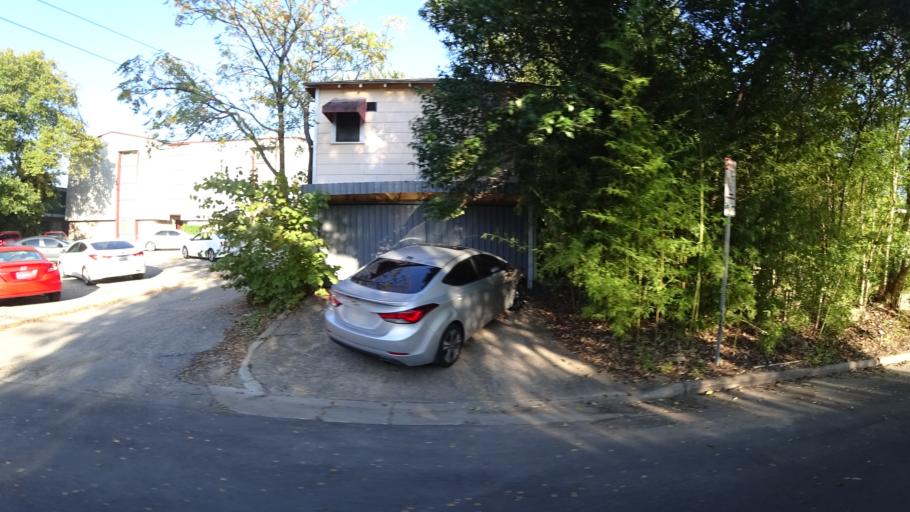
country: US
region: Texas
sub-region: Travis County
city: Austin
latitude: 30.2859
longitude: -97.7496
